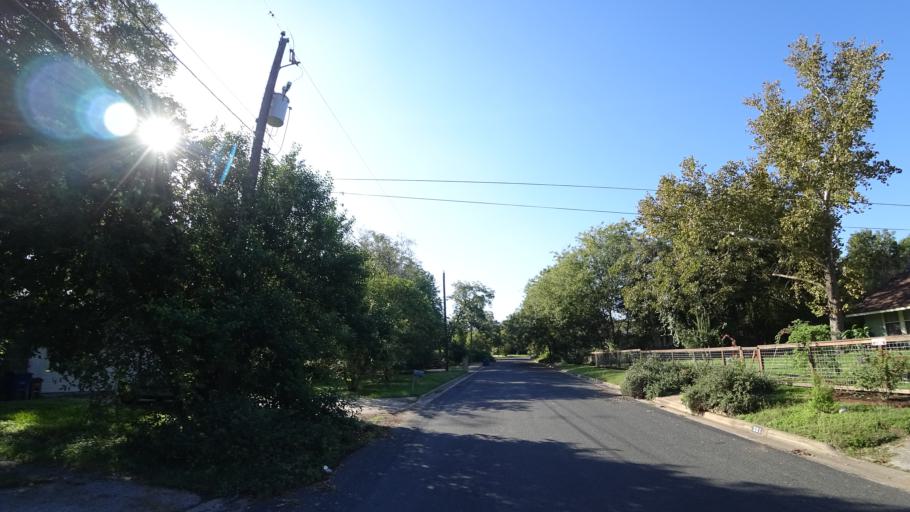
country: US
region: Texas
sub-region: Travis County
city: Austin
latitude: 30.3518
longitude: -97.6980
